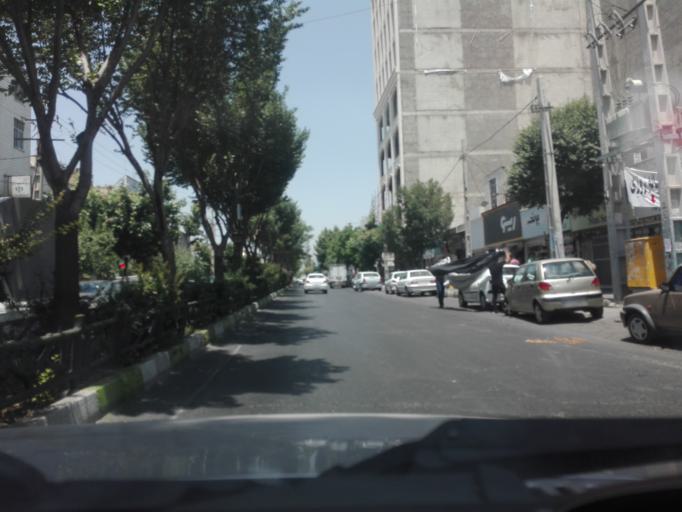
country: IR
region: Tehran
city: Shahre Jadide Andisheh
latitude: 35.7286
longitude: 50.9895
